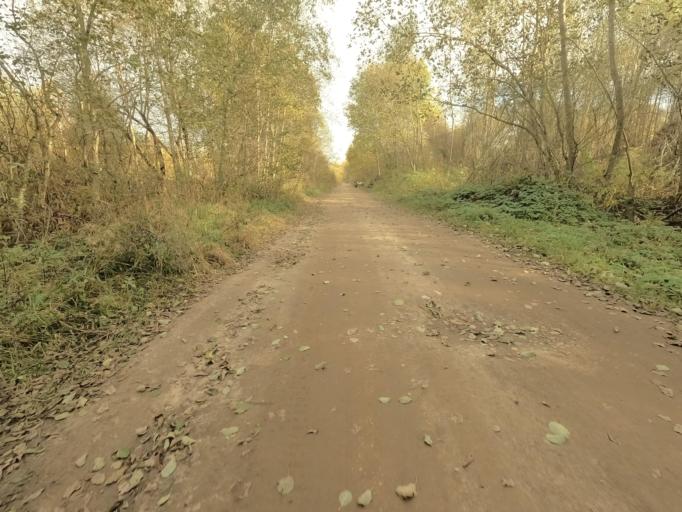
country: RU
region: Novgorod
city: Volkhovskiy
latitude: 58.8935
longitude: 31.0207
